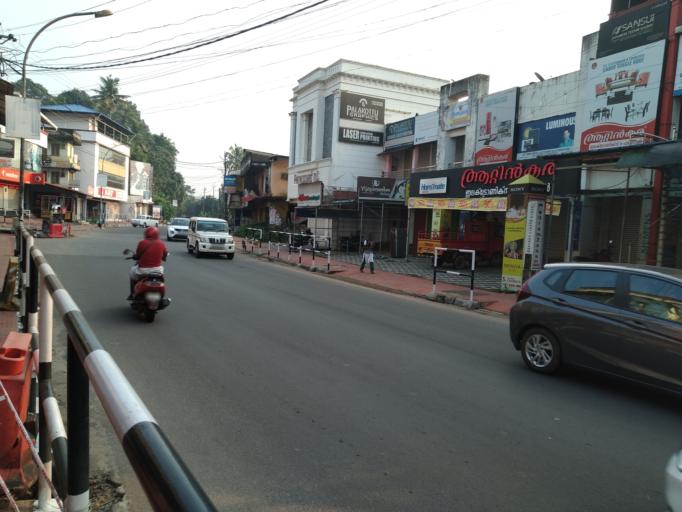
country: IN
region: Kerala
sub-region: Kollam
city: Punalur
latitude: 9.0068
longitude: 76.7834
